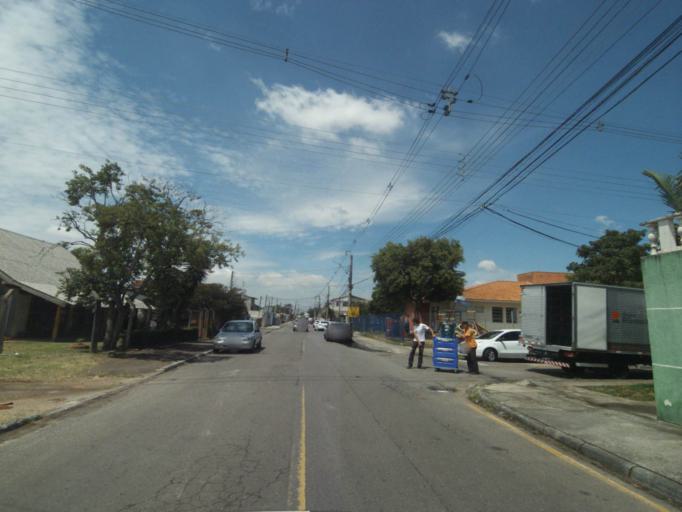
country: BR
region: Parana
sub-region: Pinhais
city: Pinhais
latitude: -25.4713
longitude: -49.1973
